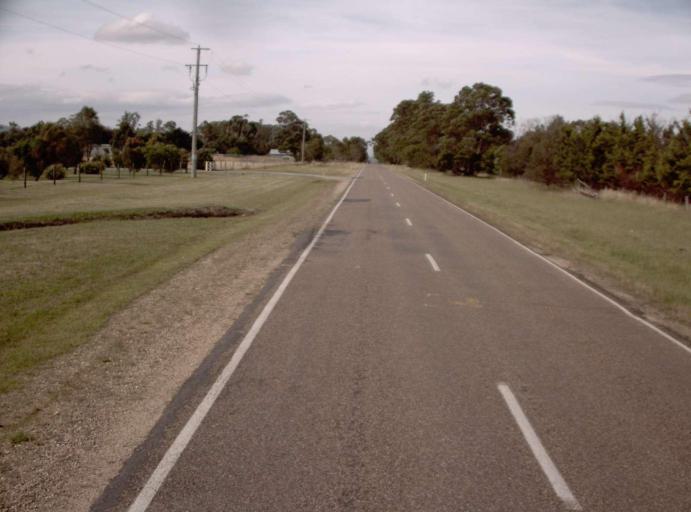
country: AU
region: Victoria
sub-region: Wellington
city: Heyfield
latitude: -38.0358
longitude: 146.6668
